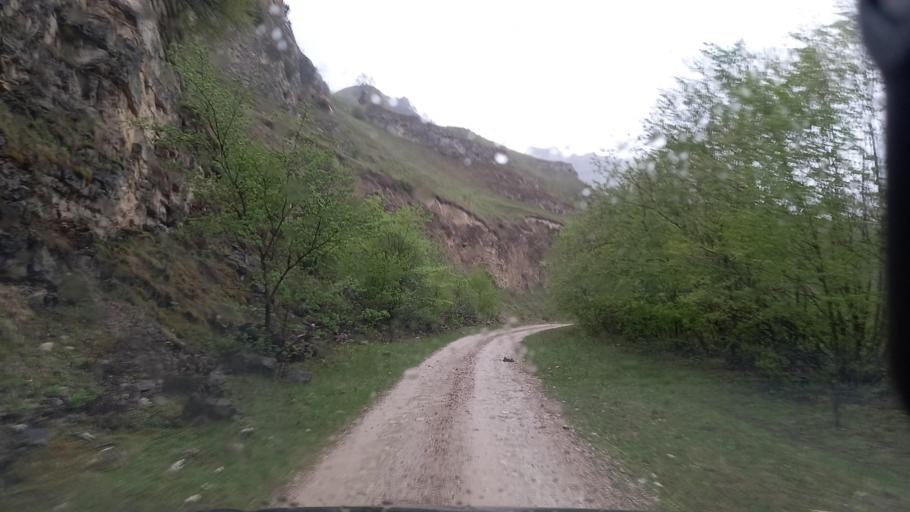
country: RU
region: Kabardino-Balkariya
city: Bylym
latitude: 43.5895
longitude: 43.0226
